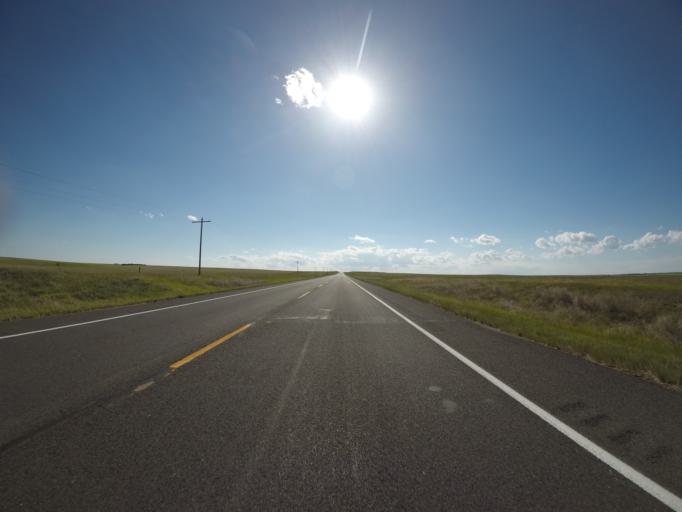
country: US
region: Colorado
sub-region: Morgan County
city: Brush
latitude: 40.6104
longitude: -103.6299
